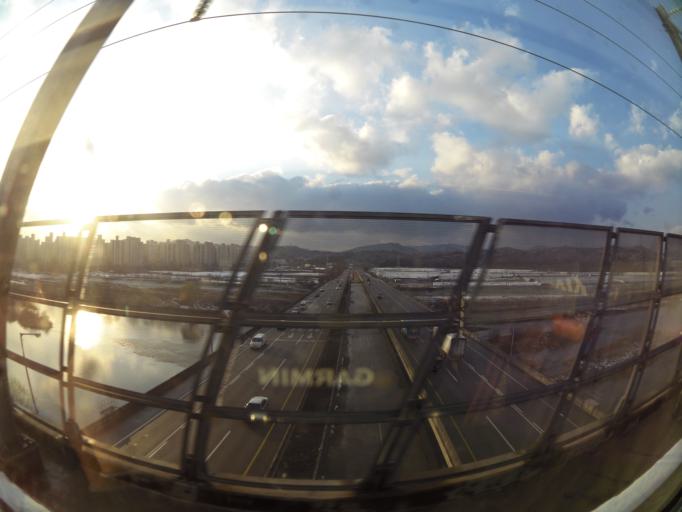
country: KR
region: Daejeon
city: Songgang-dong
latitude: 36.4046
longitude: 127.4149
